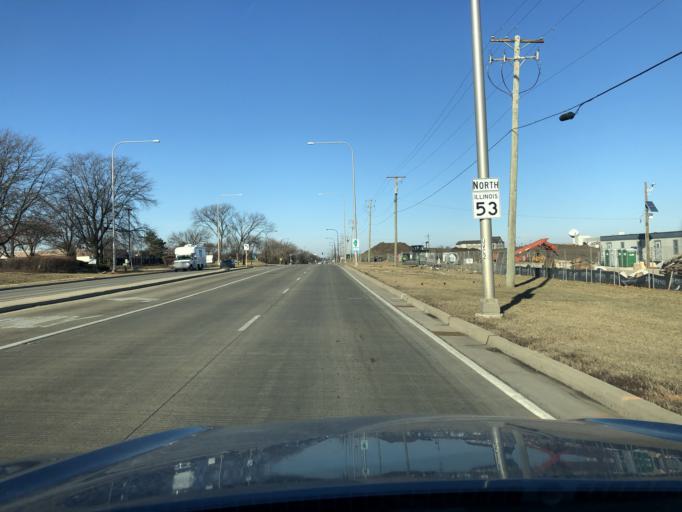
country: US
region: Illinois
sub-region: DuPage County
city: Itasca
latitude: 41.9897
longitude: -88.0313
